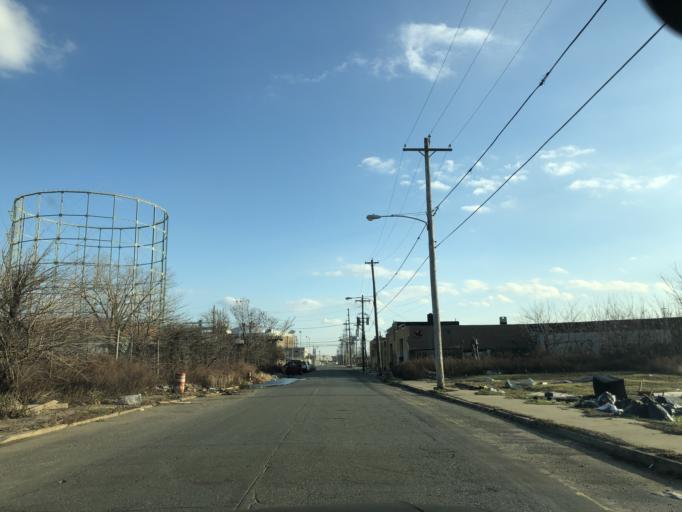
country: US
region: New Jersey
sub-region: Camden County
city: Pennsauken
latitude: 39.9859
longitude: -75.0905
